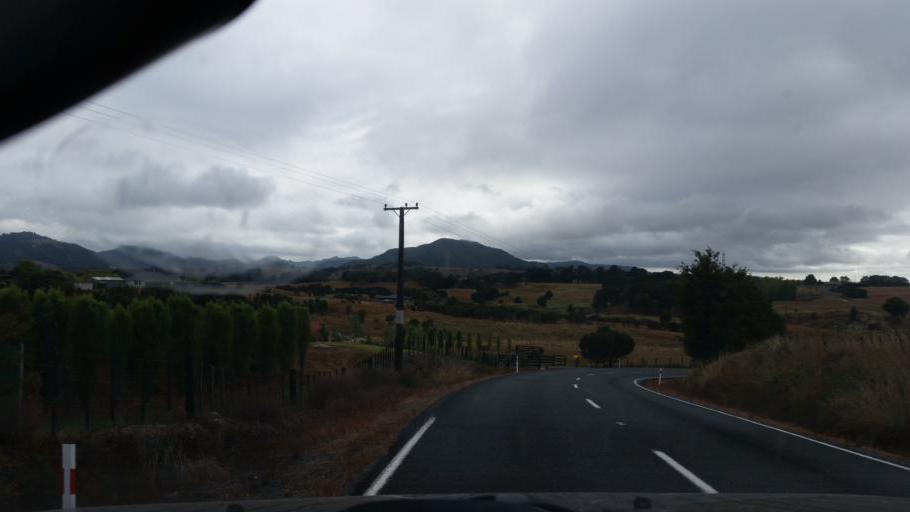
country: NZ
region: Auckland
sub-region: Auckland
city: Wellsford
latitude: -36.1701
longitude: 174.4205
